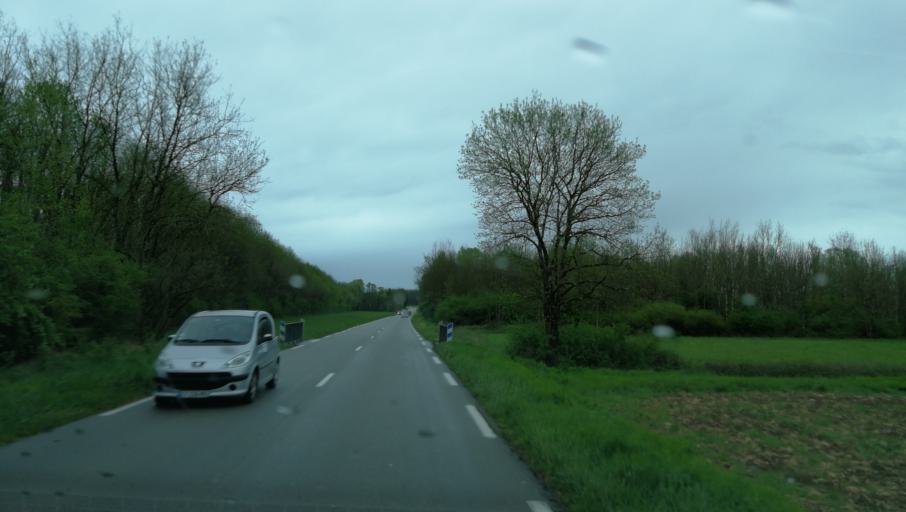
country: FR
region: Franche-Comte
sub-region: Departement du Jura
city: Bletterans
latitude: 46.7237
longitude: 5.4730
